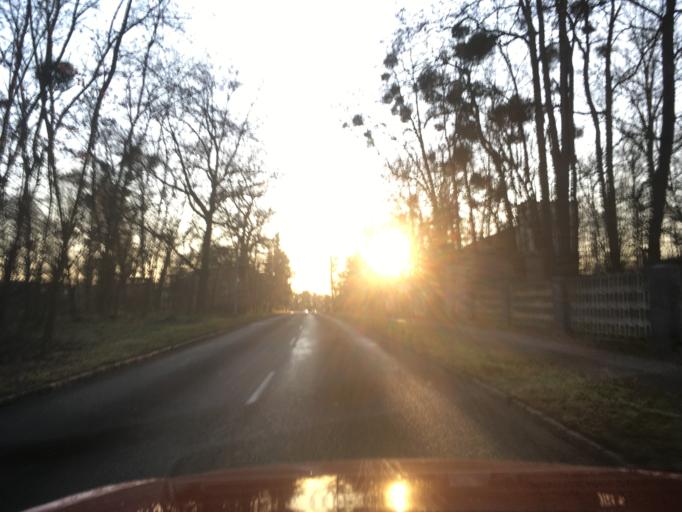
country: DE
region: Saxony-Anhalt
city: Rosslau
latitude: 51.8962
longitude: 12.2680
